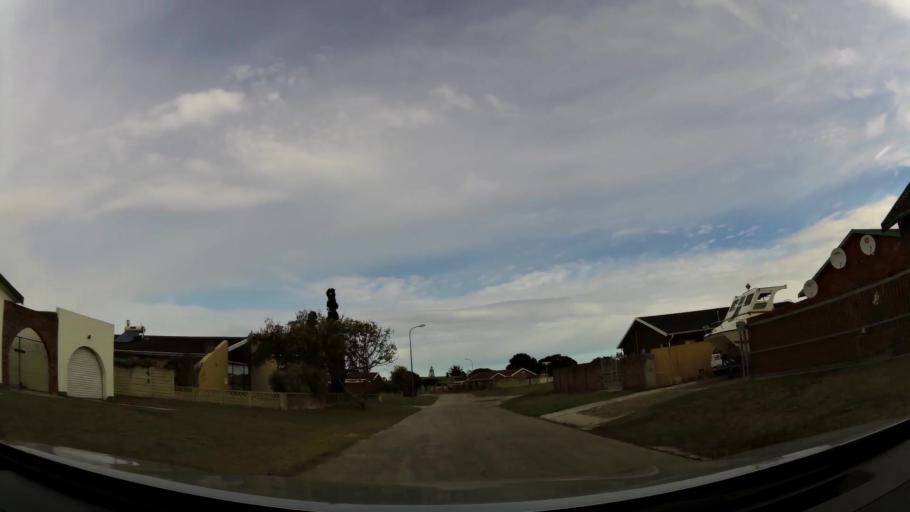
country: ZA
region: Eastern Cape
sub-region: Nelson Mandela Bay Metropolitan Municipality
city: Port Elizabeth
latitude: -33.9380
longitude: 25.4659
